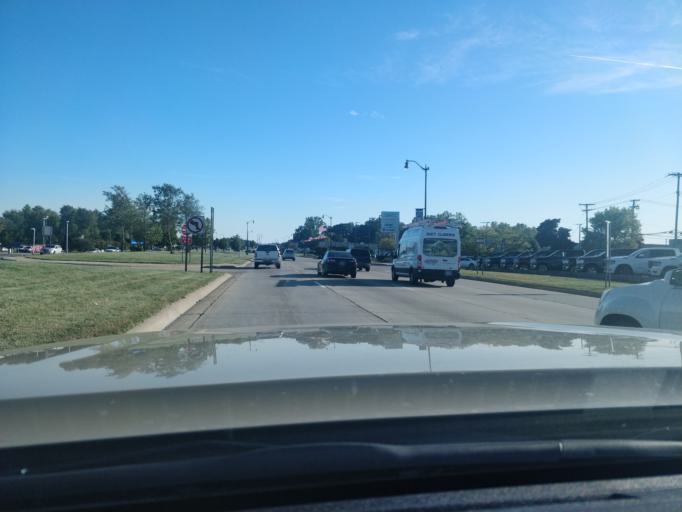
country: US
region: Michigan
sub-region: Wayne County
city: Taylor
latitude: 42.2199
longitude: -83.2690
